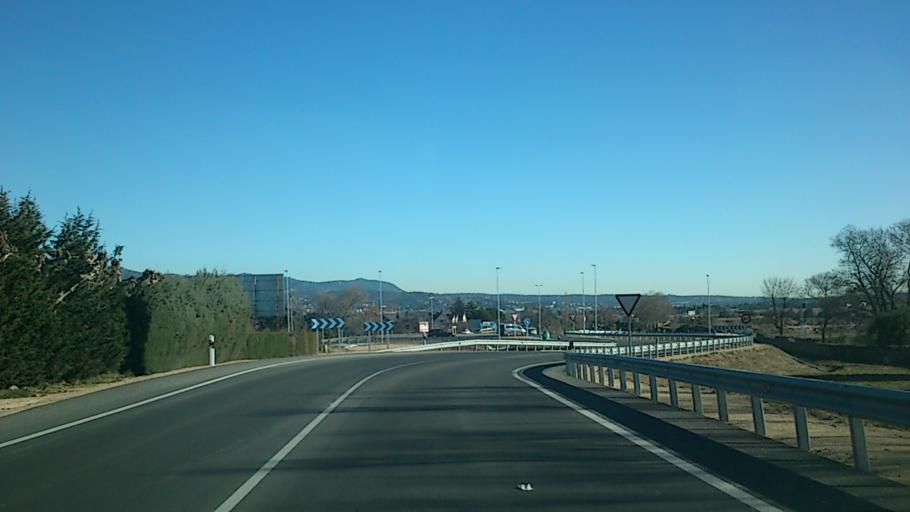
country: ES
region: Madrid
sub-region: Provincia de Madrid
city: Alpedrete
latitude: 40.6495
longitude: -4.0492
